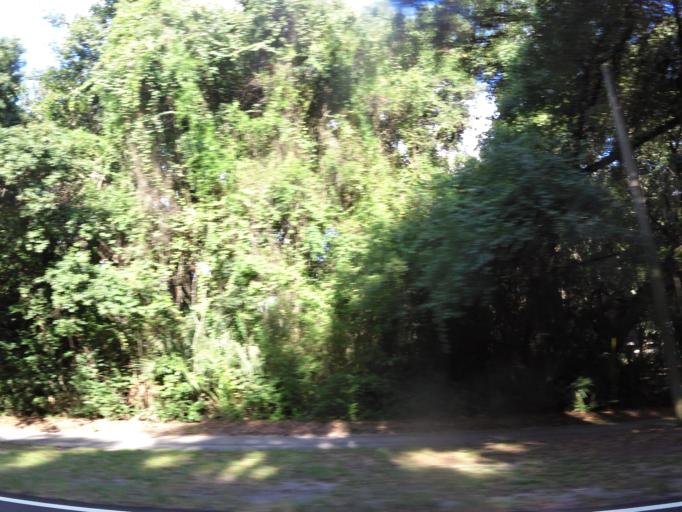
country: US
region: Georgia
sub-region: Glynn County
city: Saint Simon Mills
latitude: 31.1813
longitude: -81.3775
